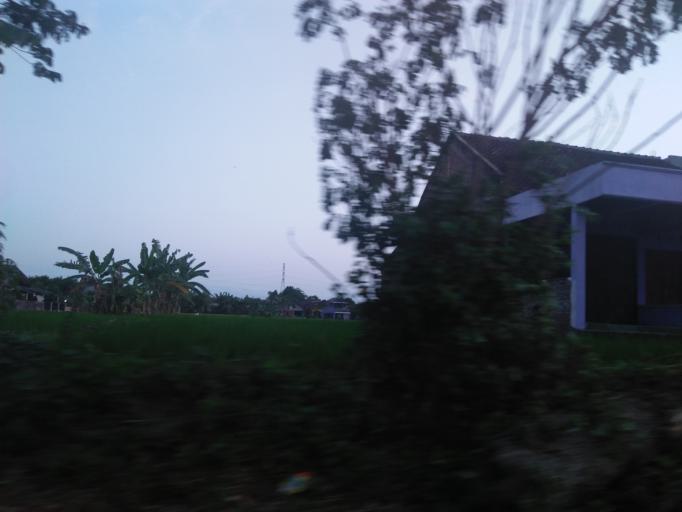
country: ID
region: Daerah Istimewa Yogyakarta
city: Sewon
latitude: -7.8437
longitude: 110.3944
